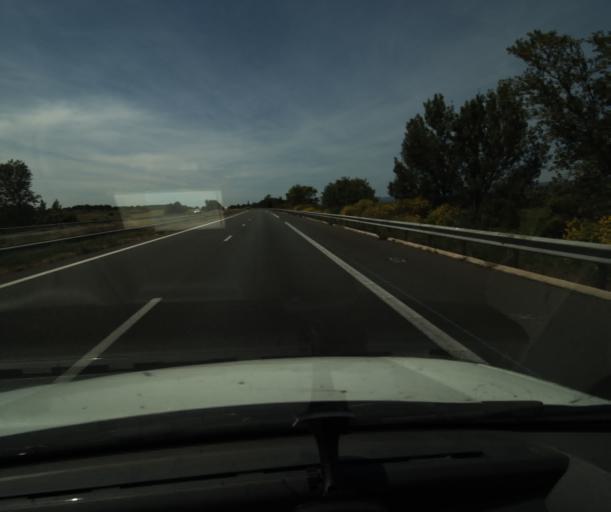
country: FR
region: Languedoc-Roussillon
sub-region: Departement de l'Aude
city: Trebes
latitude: 43.1913
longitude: 2.4582
